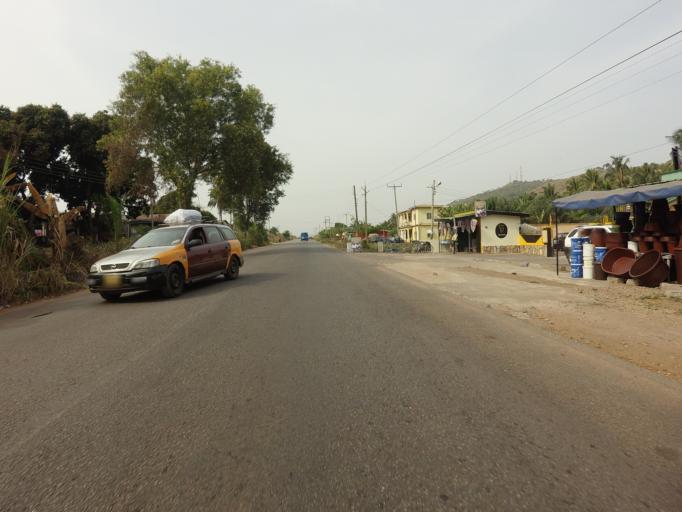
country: GH
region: Volta
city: Ho
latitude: 6.6093
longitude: 0.4576
